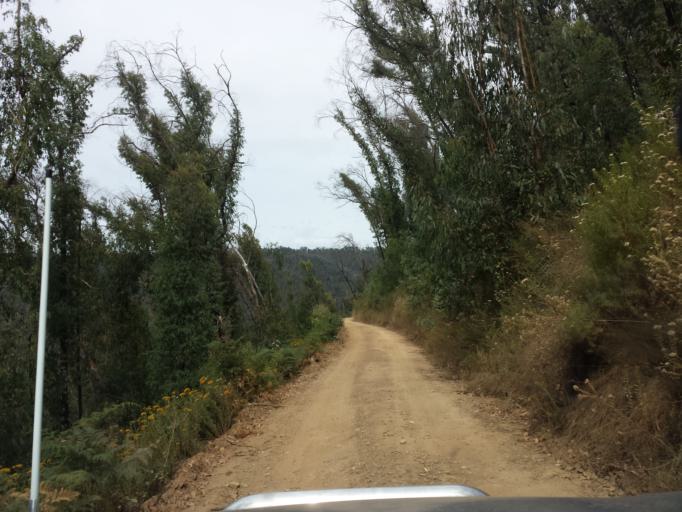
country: AU
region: Victoria
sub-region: Wellington
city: Heyfield
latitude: -37.7440
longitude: 146.4074
